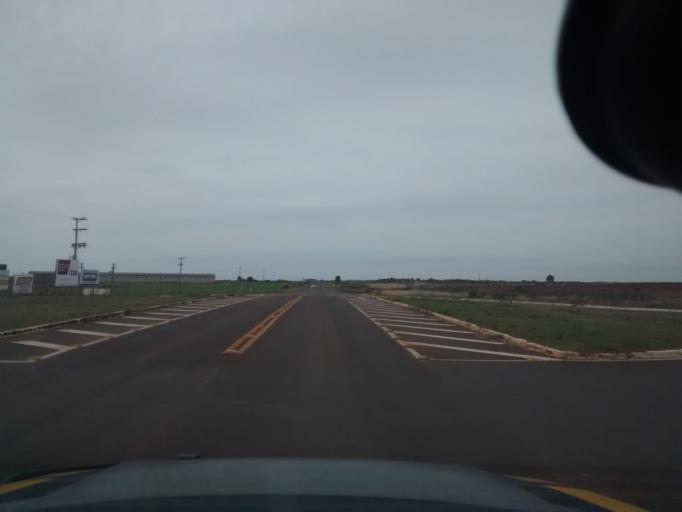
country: BR
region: Rio Grande do Sul
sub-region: Vacaria
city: Vacaria
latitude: -28.4277
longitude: -51.0241
